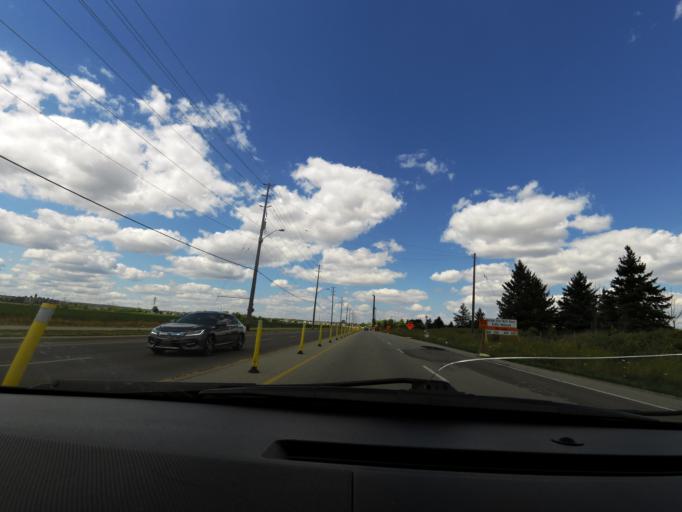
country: CA
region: Ontario
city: Burlington
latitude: 43.4032
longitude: -79.7674
